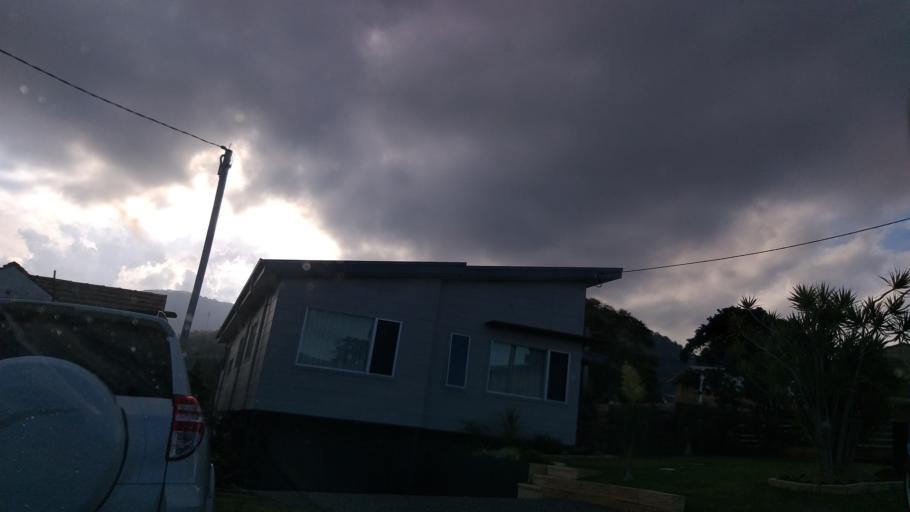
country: AU
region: New South Wales
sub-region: Wollongong
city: West Wollongong
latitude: -34.4208
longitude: 150.8605
